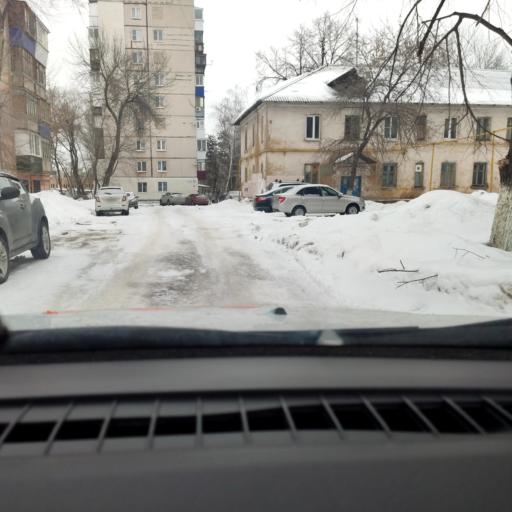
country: RU
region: Samara
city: Novokuybyshevsk
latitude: 53.0931
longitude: 49.9699
